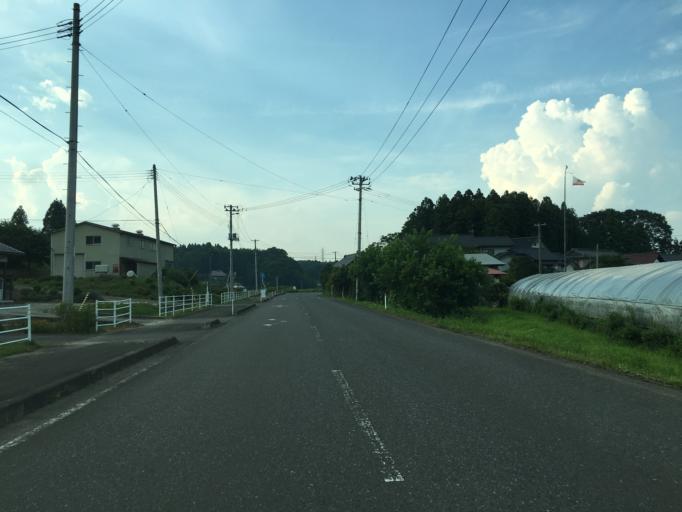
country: JP
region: Fukushima
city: Nihommatsu
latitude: 37.5603
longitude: 140.4358
